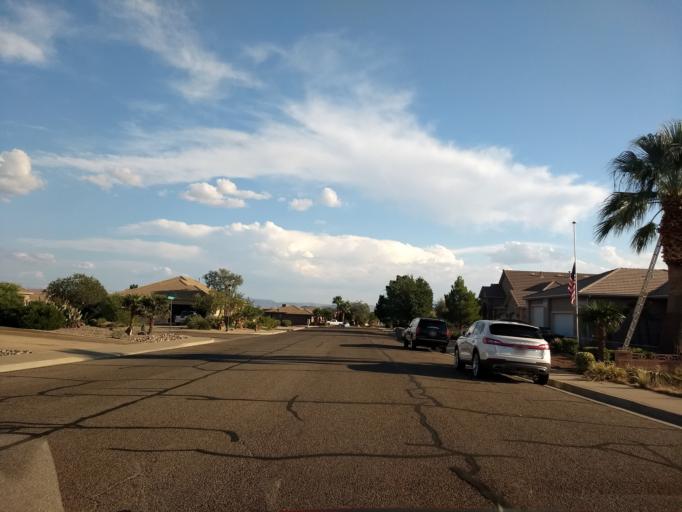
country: US
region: Utah
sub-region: Washington County
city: Saint George
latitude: 37.0971
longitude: -113.5457
